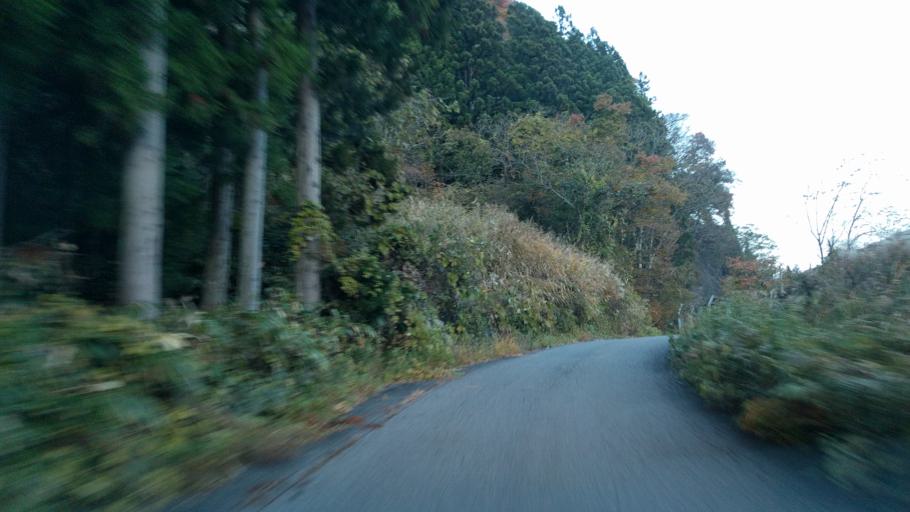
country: JP
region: Fukushima
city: Kitakata
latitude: 37.5085
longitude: 139.6894
